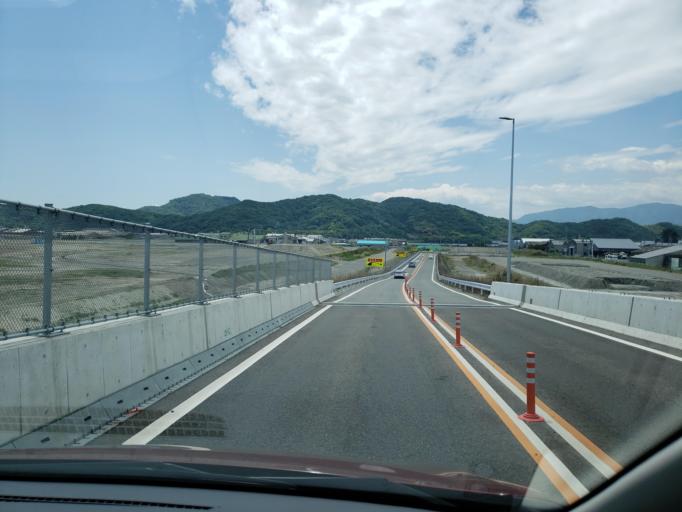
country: JP
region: Tokushima
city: Tokushima-shi
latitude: 34.0462
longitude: 134.5848
